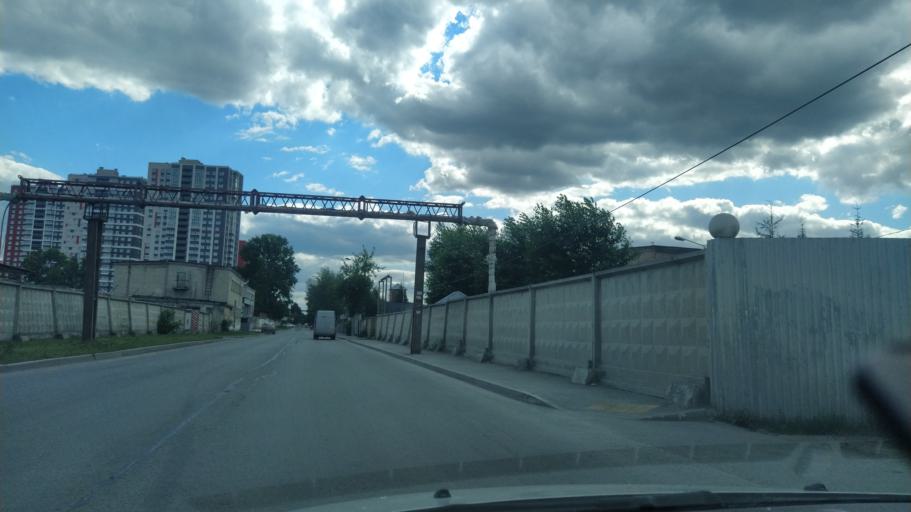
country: RU
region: Sverdlovsk
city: Shuvakish
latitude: 56.8805
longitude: 60.5270
